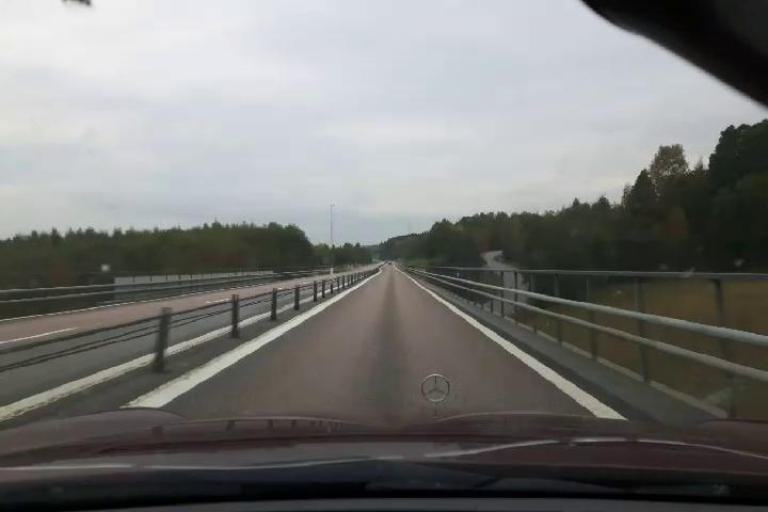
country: SE
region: Vaesternorrland
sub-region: Haernoesands Kommun
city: Haernoesand
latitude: 62.8560
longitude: 18.0170
